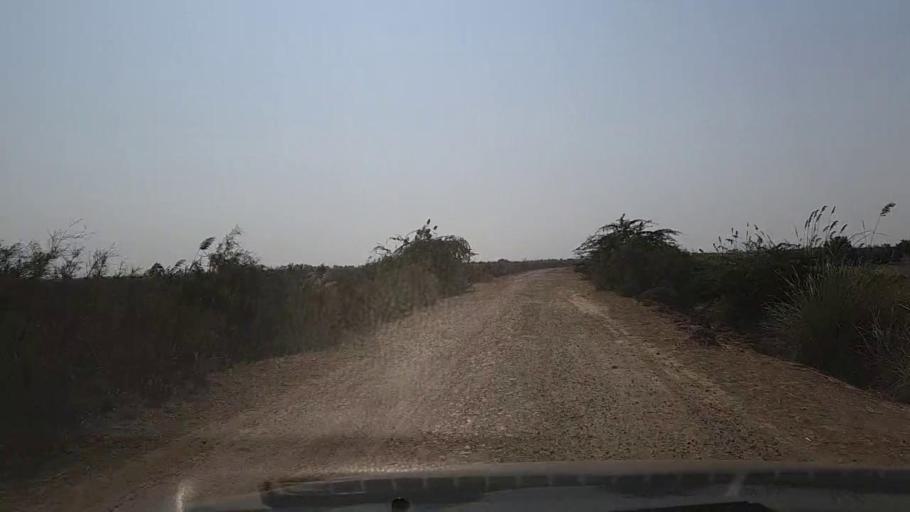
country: PK
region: Sindh
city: Mirpur Sakro
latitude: 24.3819
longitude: 67.6614
